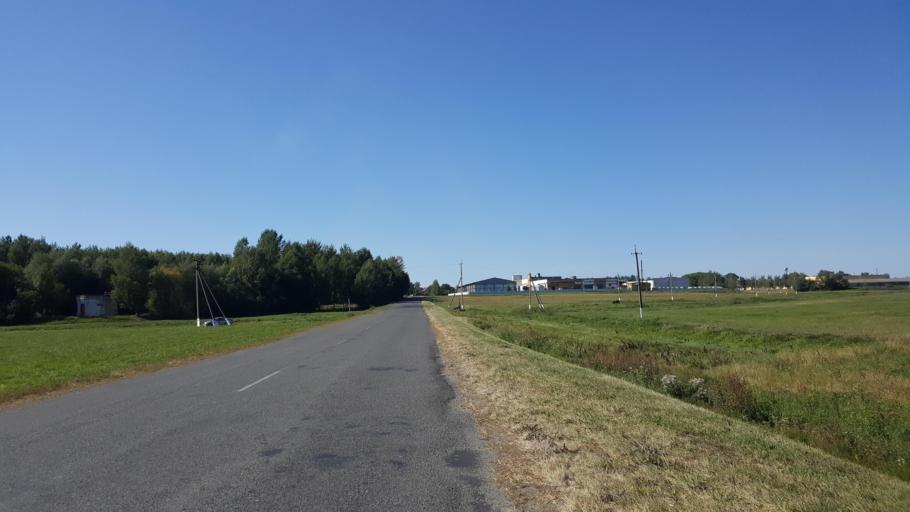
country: BY
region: Brest
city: Charnawchytsy
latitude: 52.2725
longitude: 23.5925
